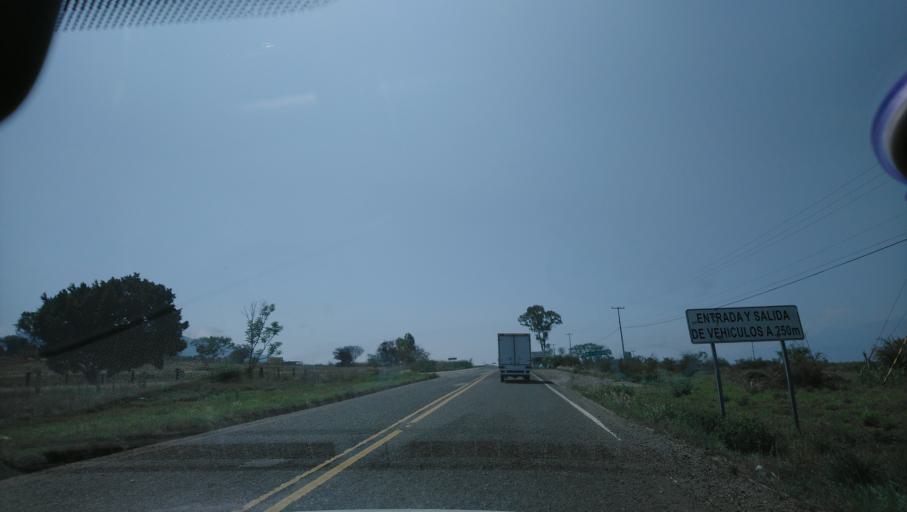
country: MX
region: Oaxaca
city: Santa Maria del Tule
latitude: 17.0386
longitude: -96.6200
